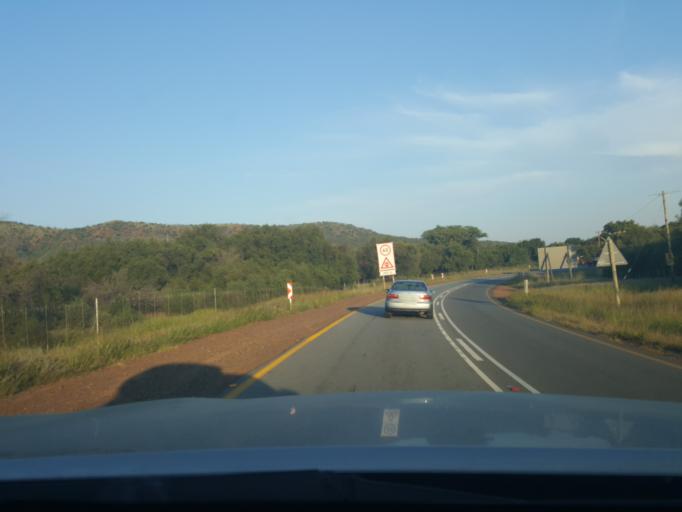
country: ZA
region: North-West
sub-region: Ngaka Modiri Molema District Municipality
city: Zeerust
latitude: -25.5233
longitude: 26.0728
